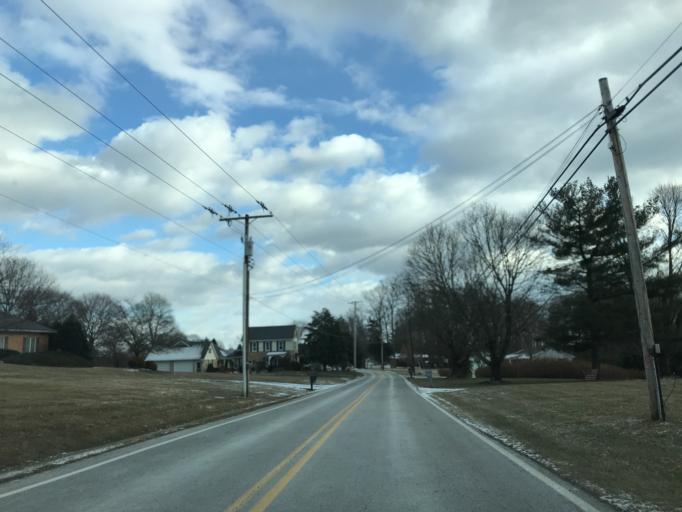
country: US
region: Maryland
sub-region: Harford County
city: Jarrettsville
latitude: 39.6280
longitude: -76.4647
